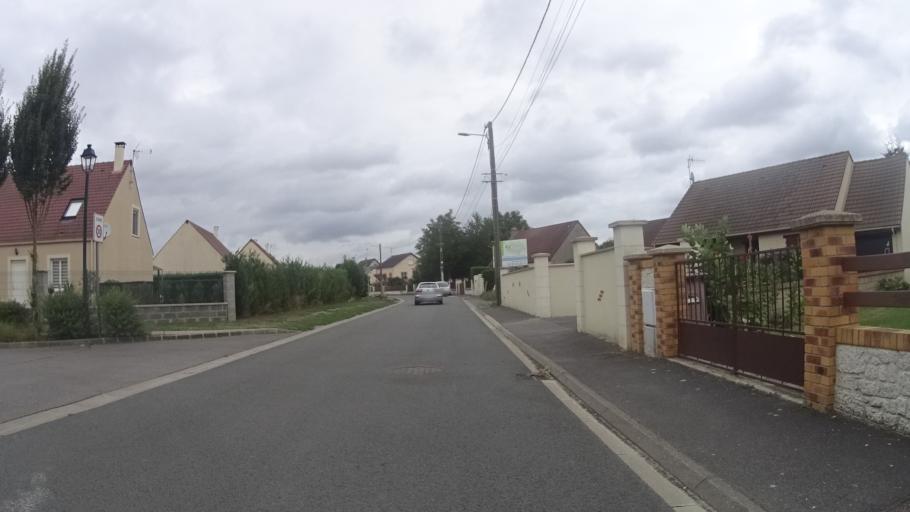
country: FR
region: Picardie
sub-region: Departement de l'Oise
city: Dreslincourt
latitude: 49.5126
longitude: 2.9463
